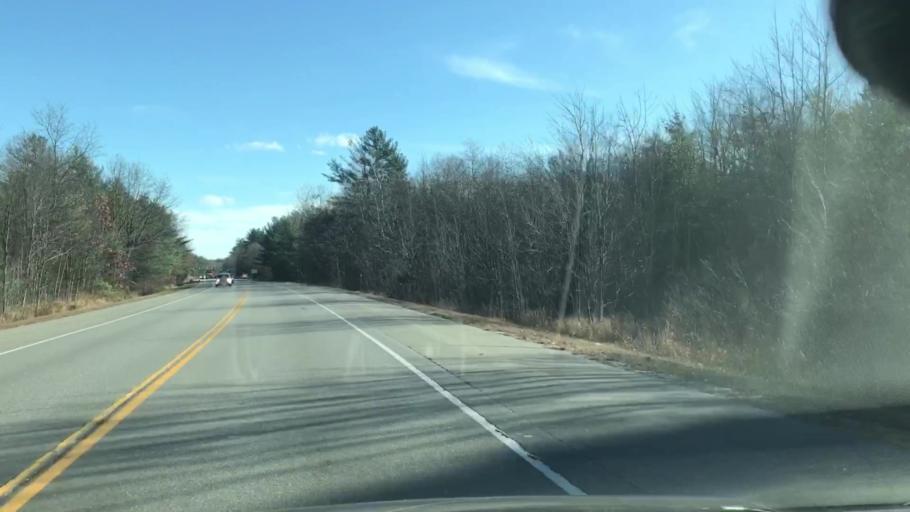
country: US
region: New Hampshire
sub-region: Hillsborough County
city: Pinardville
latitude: 42.9718
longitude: -71.5126
